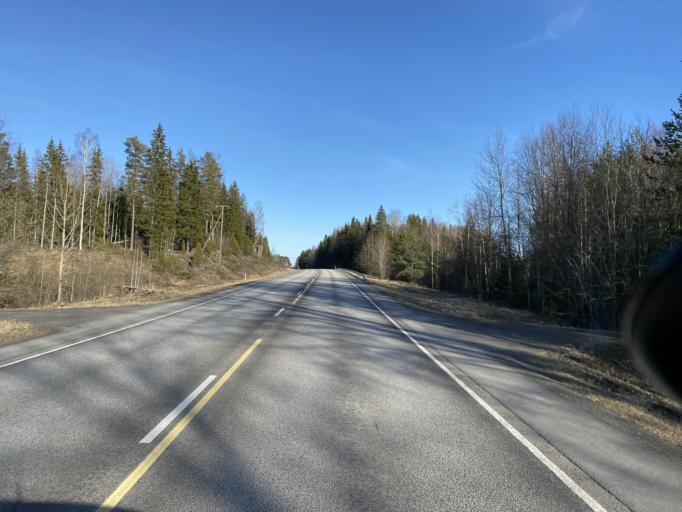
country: FI
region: Satakunta
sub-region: Rauma
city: Kiukainen
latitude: 61.1313
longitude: 22.0079
